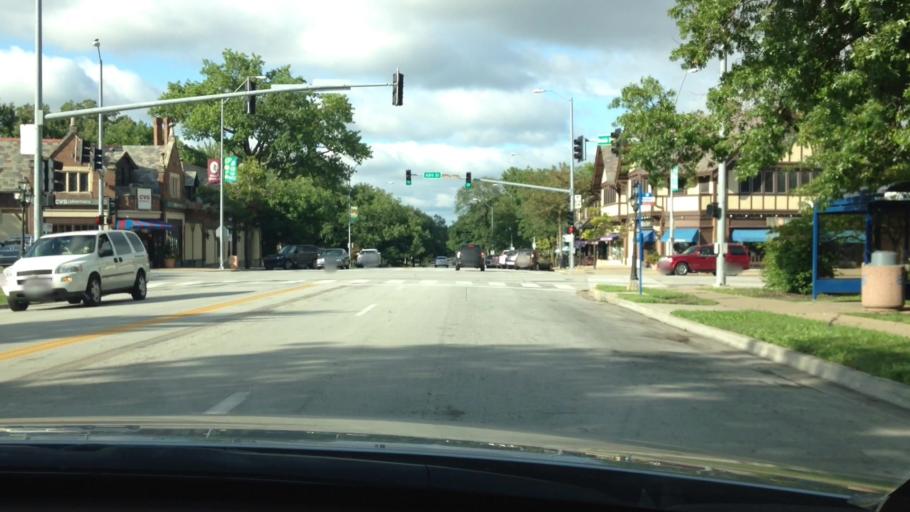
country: US
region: Kansas
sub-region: Johnson County
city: Mission Hills
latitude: 39.0136
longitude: -94.5917
